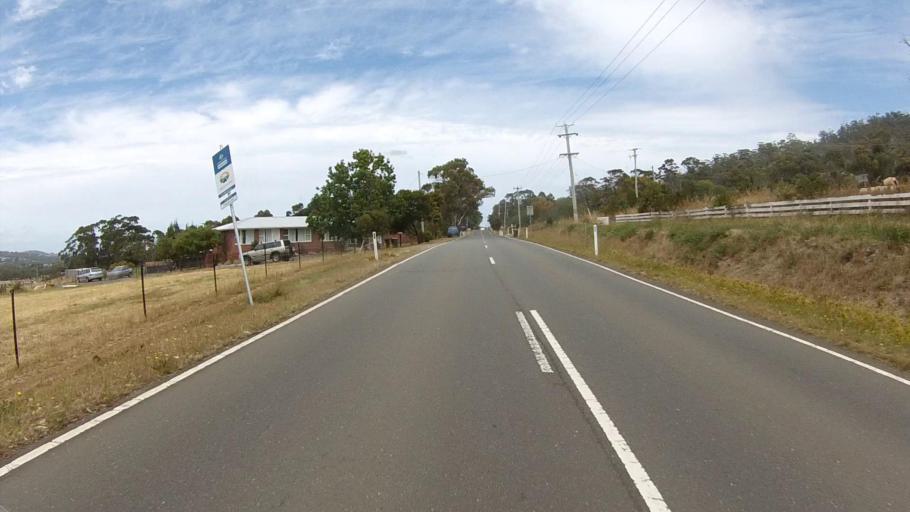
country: AU
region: Tasmania
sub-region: Clarence
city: Acton Park
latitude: -42.8940
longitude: 147.4816
